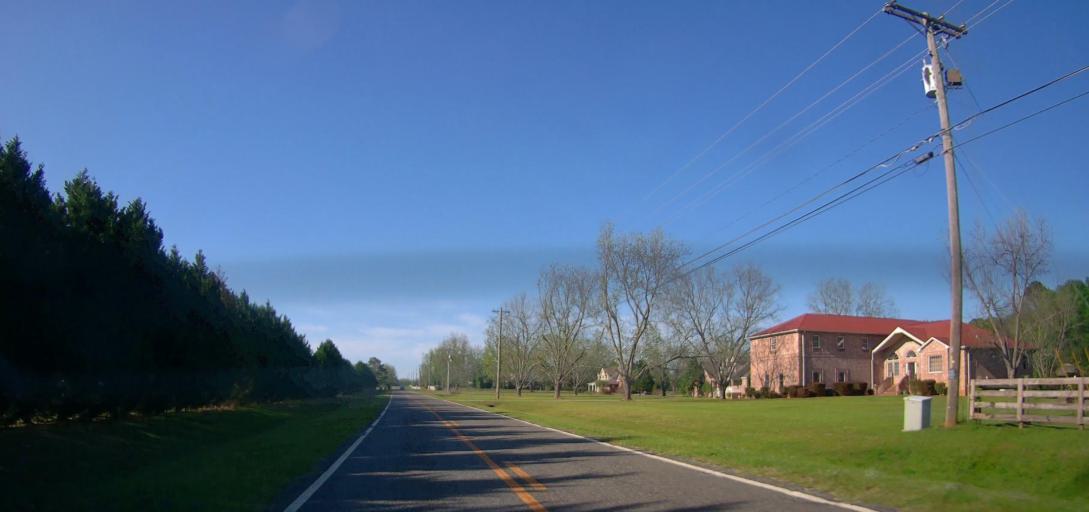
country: US
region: Georgia
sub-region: Houston County
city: Perry
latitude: 32.4691
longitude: -83.8055
